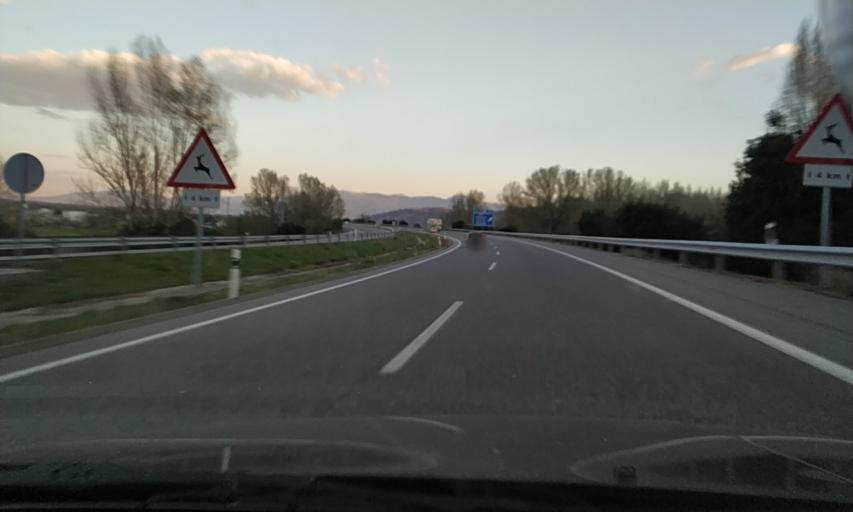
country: ES
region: Castille and Leon
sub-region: Provincia de Leon
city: Villafranca del Bierzo
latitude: 42.6000
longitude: -6.8156
